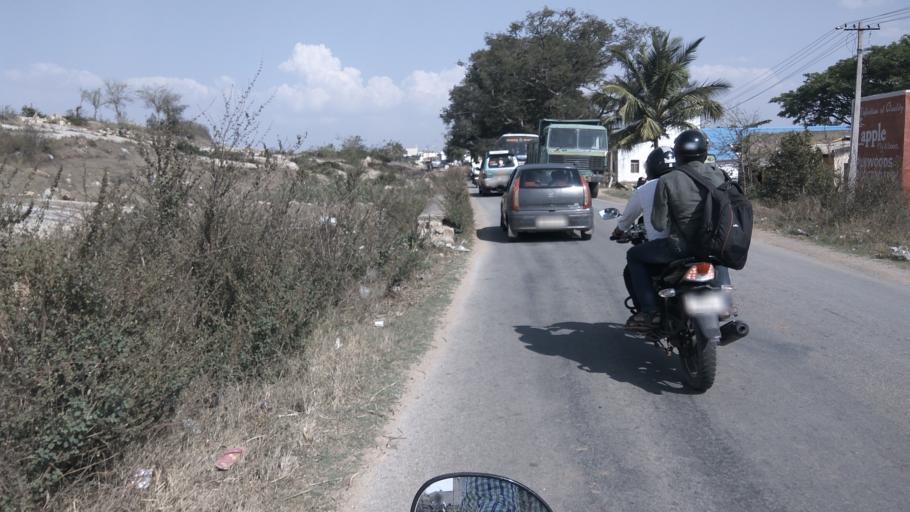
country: IN
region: Karnataka
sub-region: Kolar
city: Mulbagal
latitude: 13.1627
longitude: 78.3789
